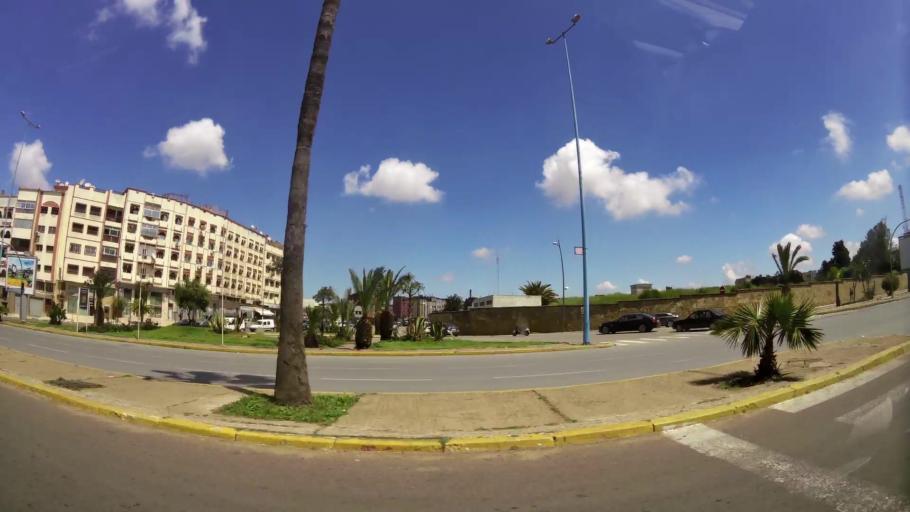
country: MA
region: Grand Casablanca
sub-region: Casablanca
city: Casablanca
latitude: 33.5507
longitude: -7.5887
